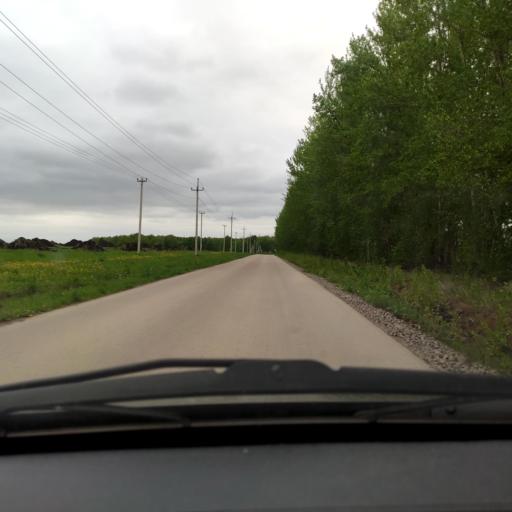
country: RU
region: Bashkortostan
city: Kabakovo
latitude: 54.6169
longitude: 56.1590
